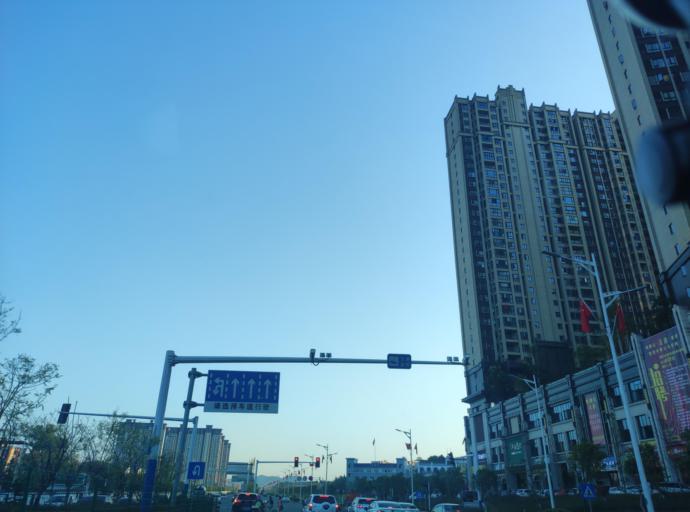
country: CN
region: Jiangxi Sheng
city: Pingxiang
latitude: 27.6316
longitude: 113.8297
